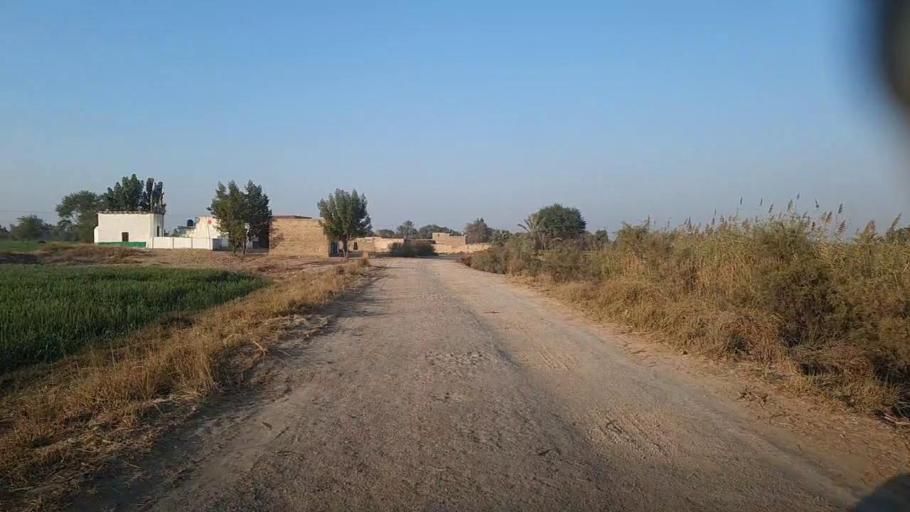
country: PK
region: Sindh
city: Mirpur Mathelo
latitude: 27.8785
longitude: 69.6496
